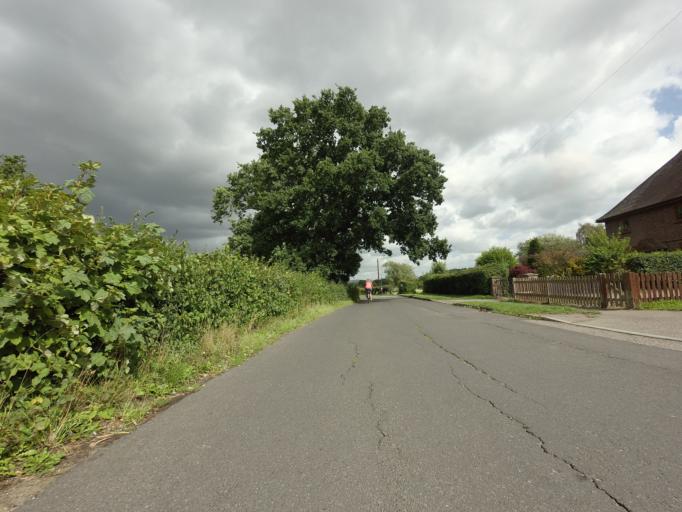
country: GB
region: England
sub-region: Kent
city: Sevenoaks
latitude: 51.2952
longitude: 0.1751
